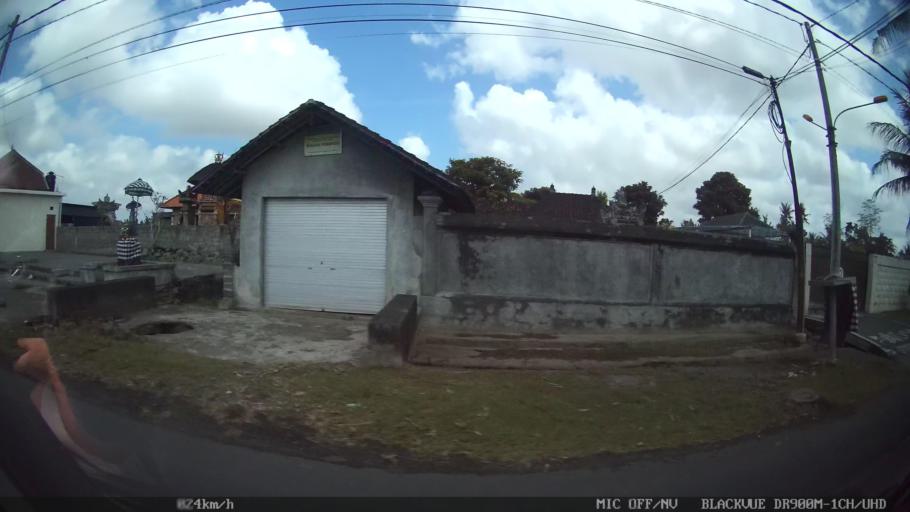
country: ID
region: Bali
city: Banjar Sedang
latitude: -8.5687
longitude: 115.2859
